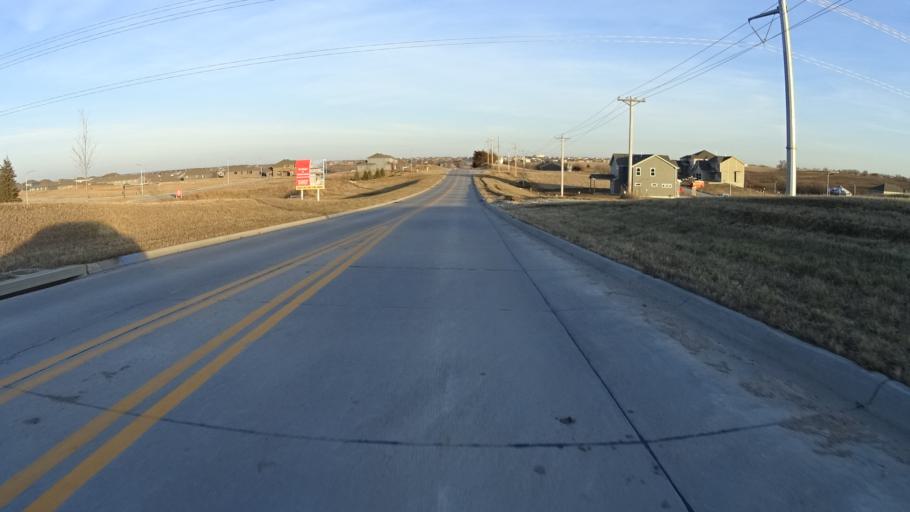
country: US
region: Nebraska
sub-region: Sarpy County
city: Papillion
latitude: 41.1326
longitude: -96.0891
